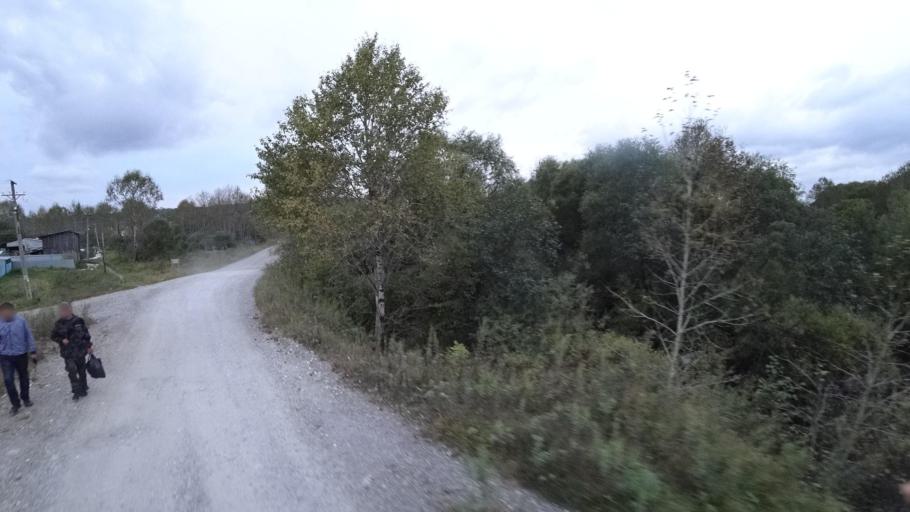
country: RU
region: Jewish Autonomous Oblast
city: Izvestkovyy
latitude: 48.9906
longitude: 131.5552
